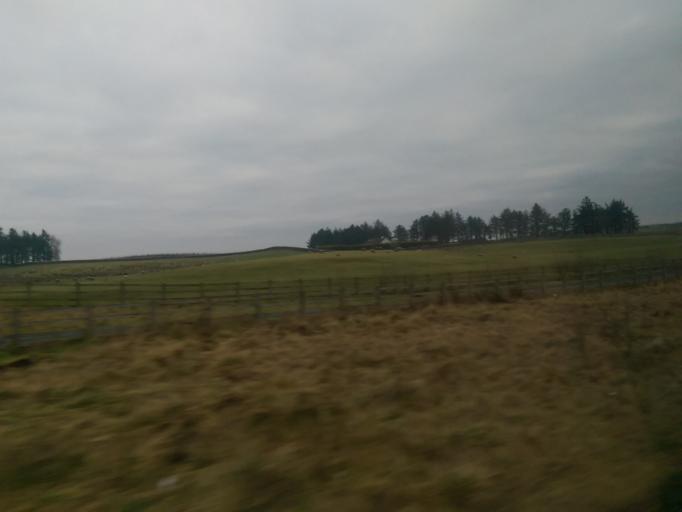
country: IE
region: Connaught
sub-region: County Galway
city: Loughrea
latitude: 53.2823
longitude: -8.4436
